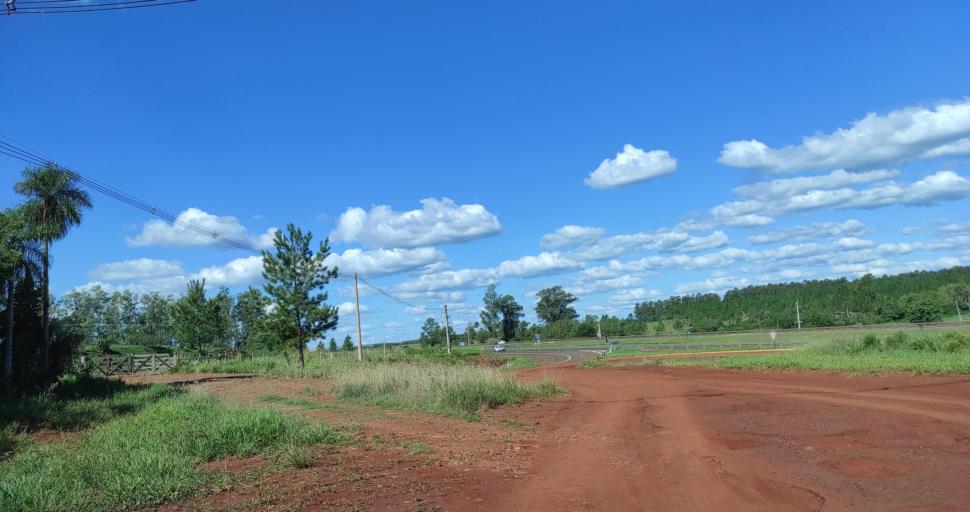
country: AR
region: Misiones
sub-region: Departamento de Candelaria
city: Candelaria
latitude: -27.4651
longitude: -55.7120
